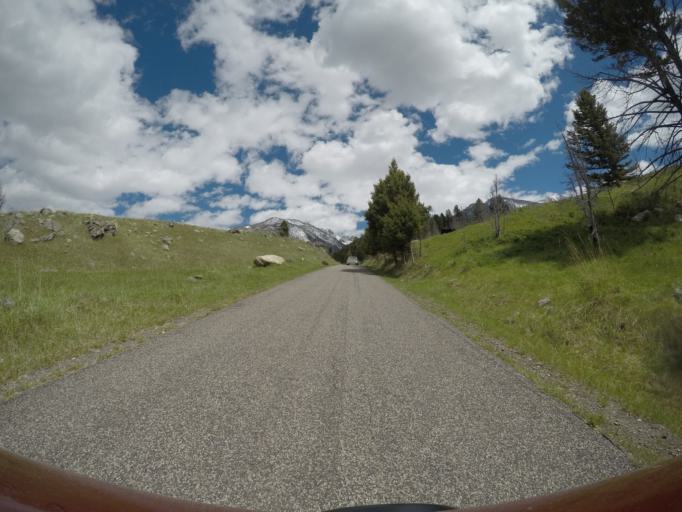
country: US
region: Montana
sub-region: Park County
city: Livingston
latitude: 45.4997
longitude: -110.5494
